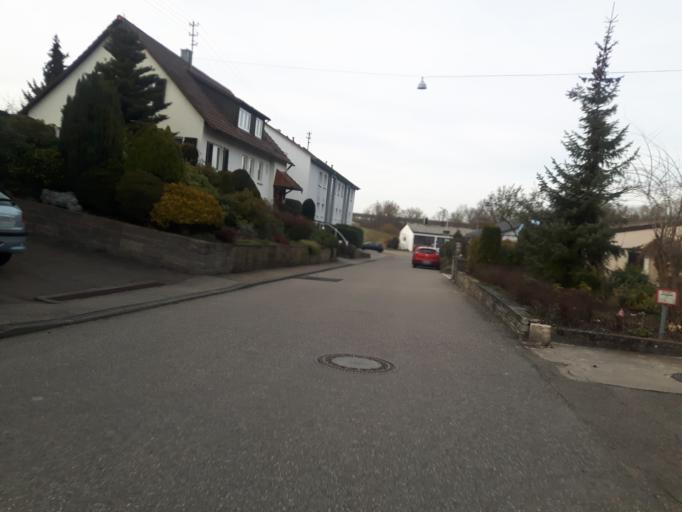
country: DE
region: Baden-Wuerttemberg
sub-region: Regierungsbezirk Stuttgart
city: Bretzfeld
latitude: 49.1911
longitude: 9.4406
